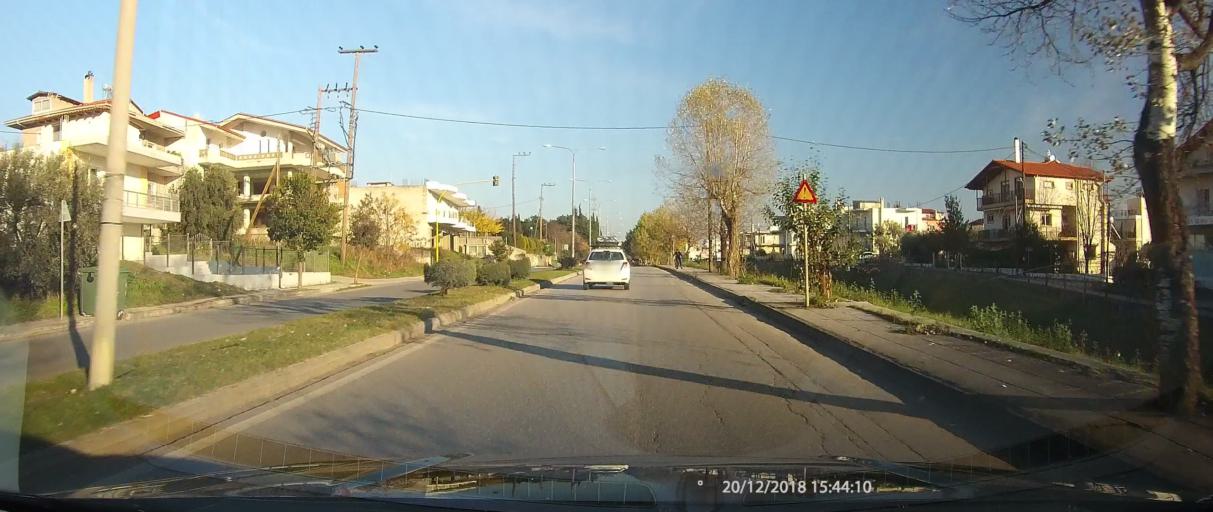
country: GR
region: Central Greece
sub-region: Nomos Fthiotidos
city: Lamia
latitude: 38.8930
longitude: 22.4162
